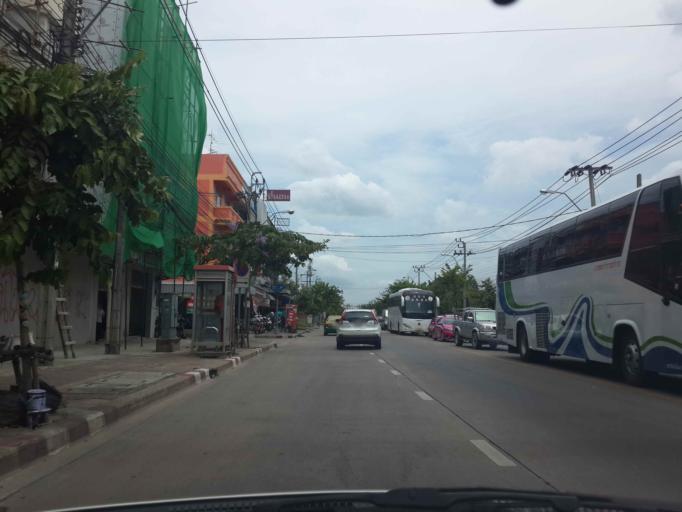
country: TH
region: Bangkok
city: Khan Na Yao
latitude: 13.8499
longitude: 100.6675
